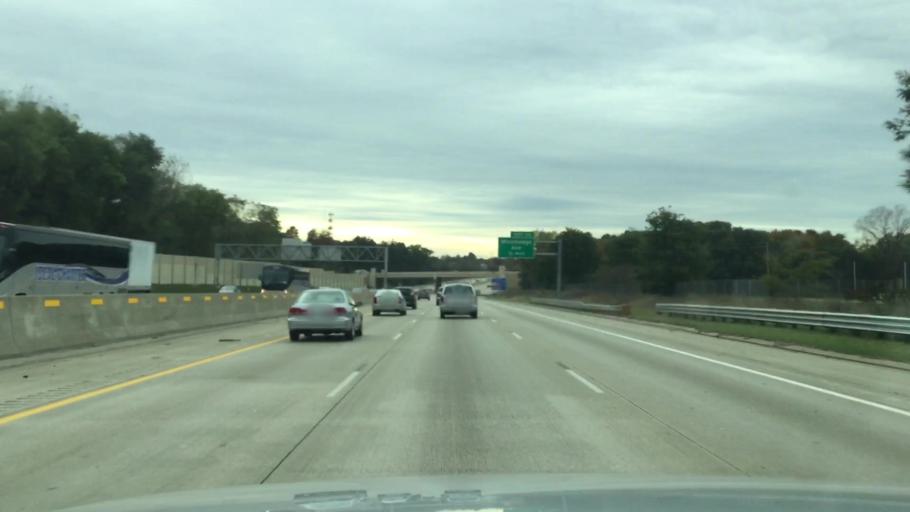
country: US
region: Michigan
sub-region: Kalamazoo County
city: Portage
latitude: 42.2405
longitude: -85.5713
